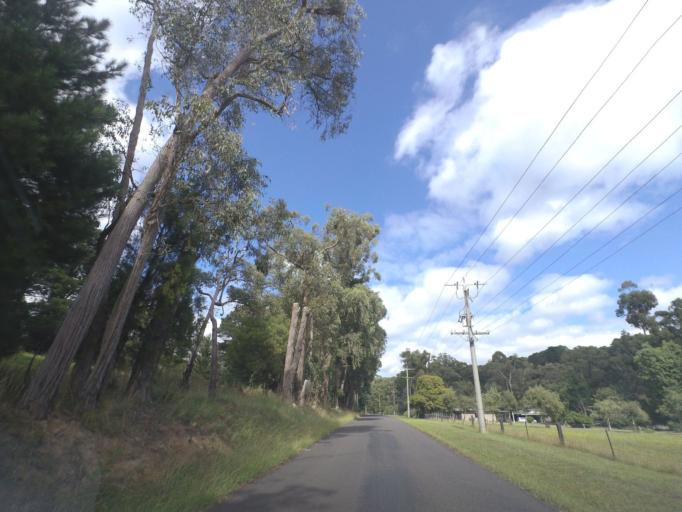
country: AU
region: Victoria
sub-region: Yarra Ranges
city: Mount Evelyn
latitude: -37.7913
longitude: 145.4043
